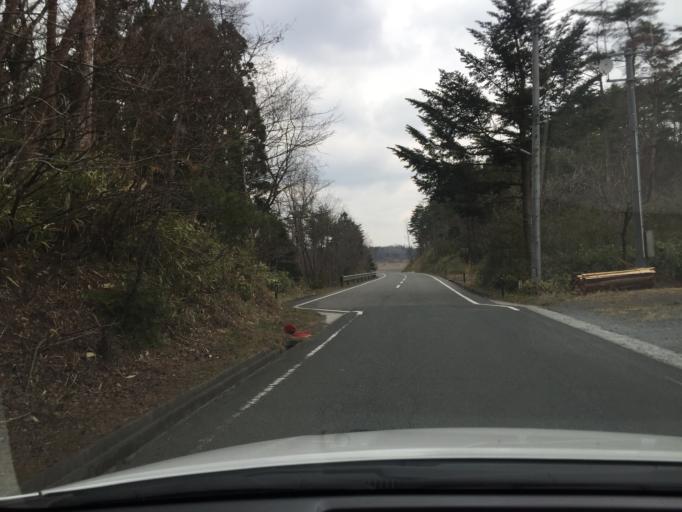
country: JP
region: Miyagi
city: Marumori
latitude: 37.7826
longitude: 140.8893
